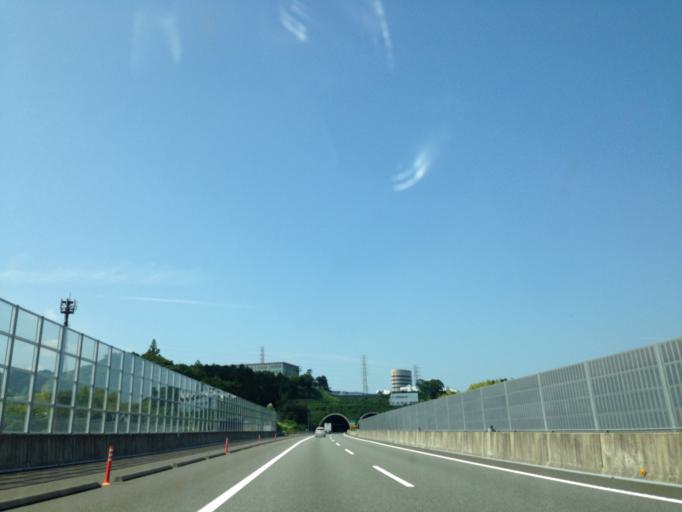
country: JP
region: Shizuoka
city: Gotemba
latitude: 35.2204
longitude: 138.8879
